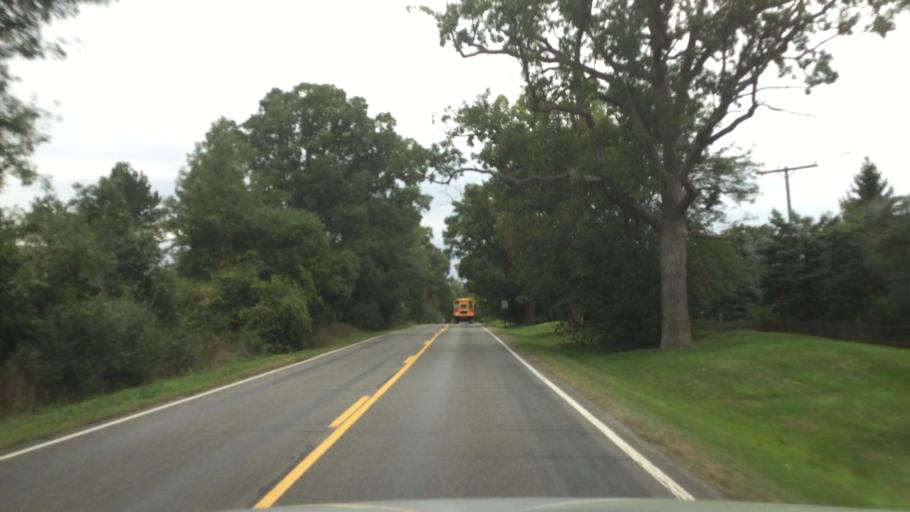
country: US
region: Michigan
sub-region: Livingston County
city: Brighton
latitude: 42.4873
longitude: -83.7677
